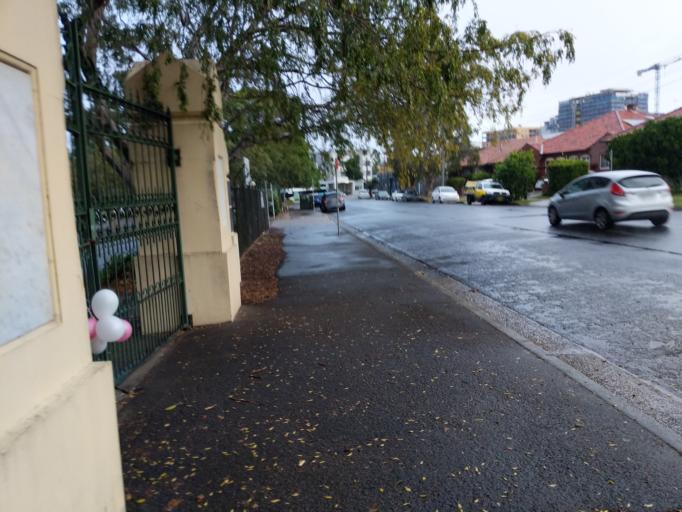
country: AU
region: New South Wales
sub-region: Ashfield
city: Croydon
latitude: -33.8682
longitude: 151.1084
